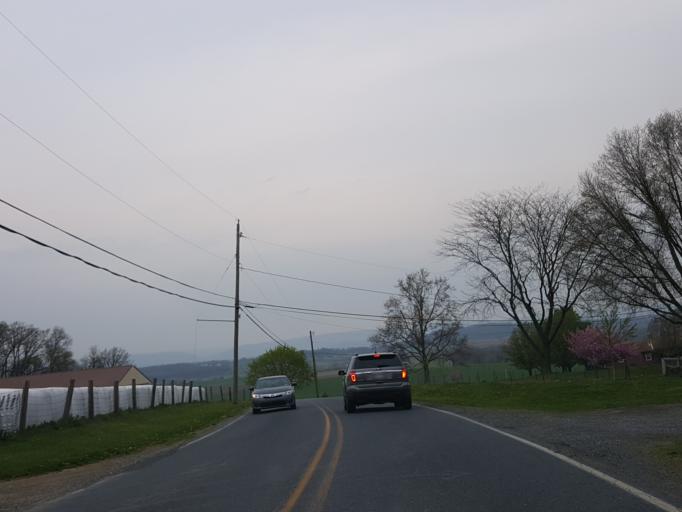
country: US
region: Pennsylvania
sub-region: Lebanon County
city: Cleona
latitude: 40.3482
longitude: -76.4926
